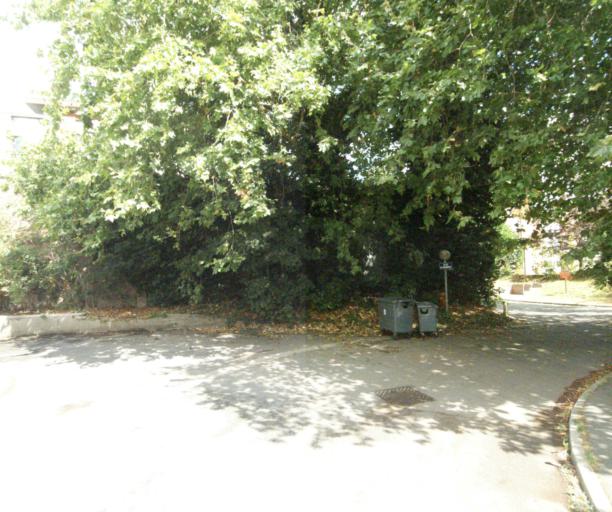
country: FR
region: Nord-Pas-de-Calais
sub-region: Departement du Nord
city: Croix
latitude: 50.6723
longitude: 3.1530
